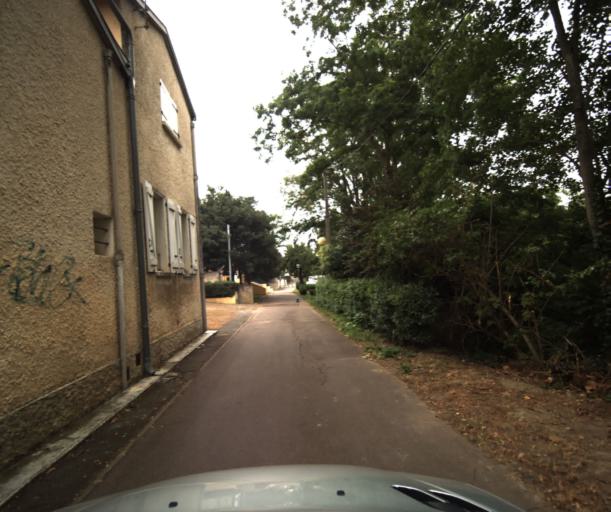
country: FR
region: Midi-Pyrenees
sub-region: Departement de la Haute-Garonne
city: Portet-sur-Garonne
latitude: 43.5202
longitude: 1.4071
